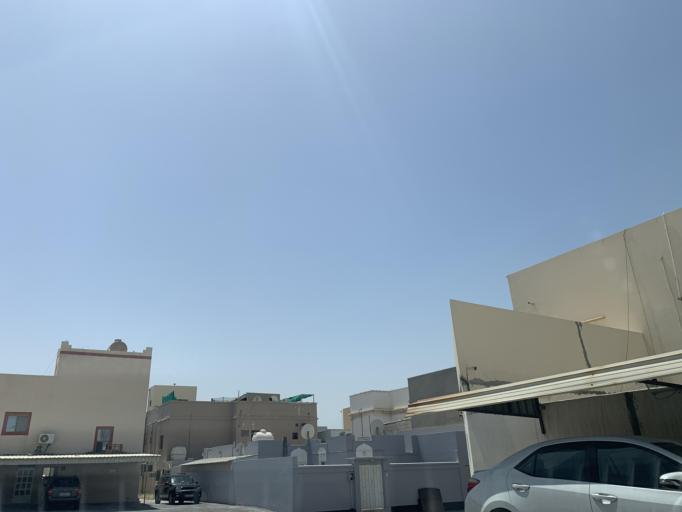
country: BH
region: Northern
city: Ar Rifa'
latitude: 26.1386
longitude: 50.5684
